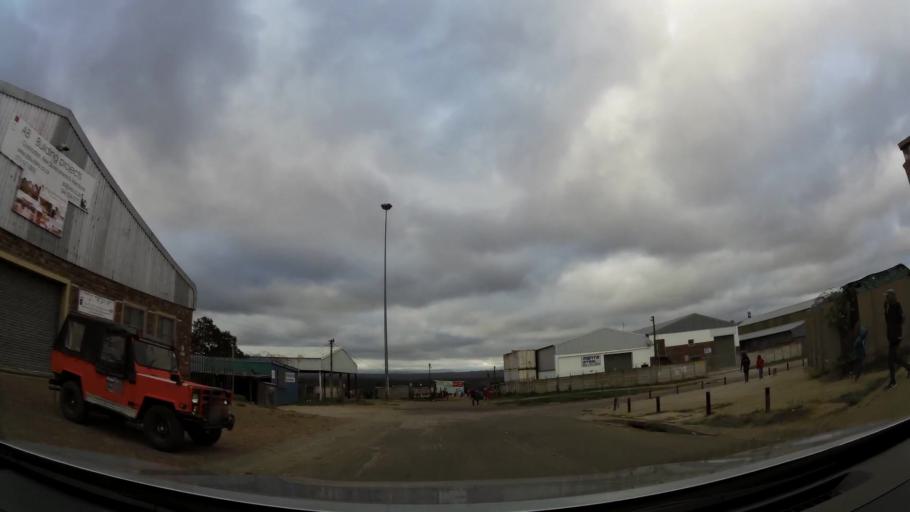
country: ZA
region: Western Cape
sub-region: Eden District Municipality
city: Plettenberg Bay
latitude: -34.0487
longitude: 23.3534
